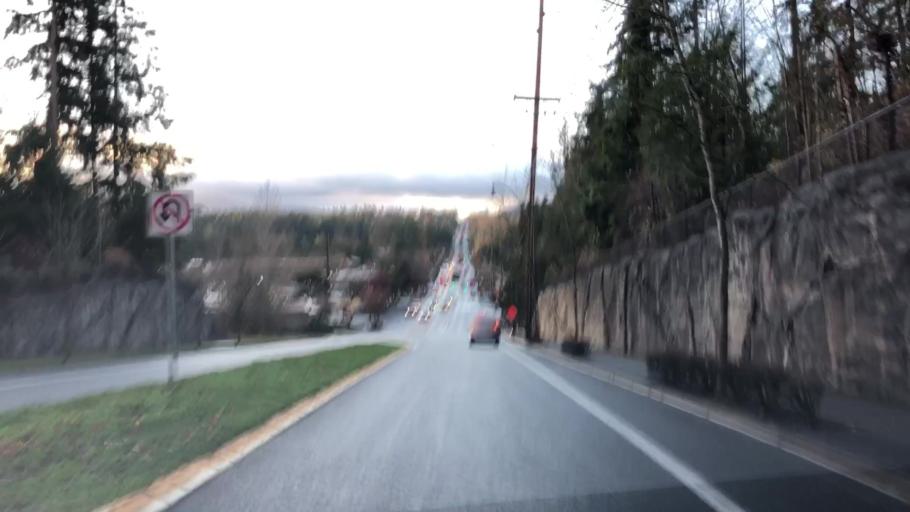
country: US
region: Washington
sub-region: King County
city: City of Sammamish
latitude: 47.6182
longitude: -122.0357
